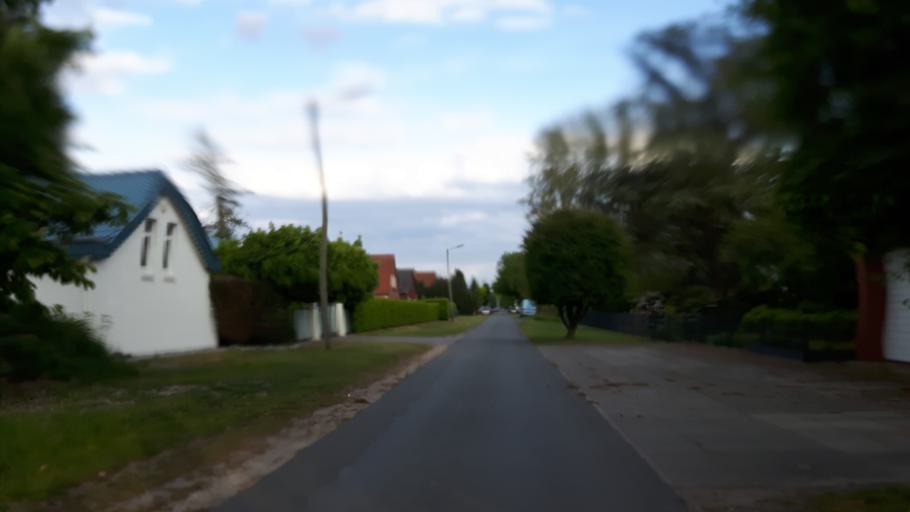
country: DE
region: Lower Saxony
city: Gross Ippener
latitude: 53.0134
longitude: 8.5961
